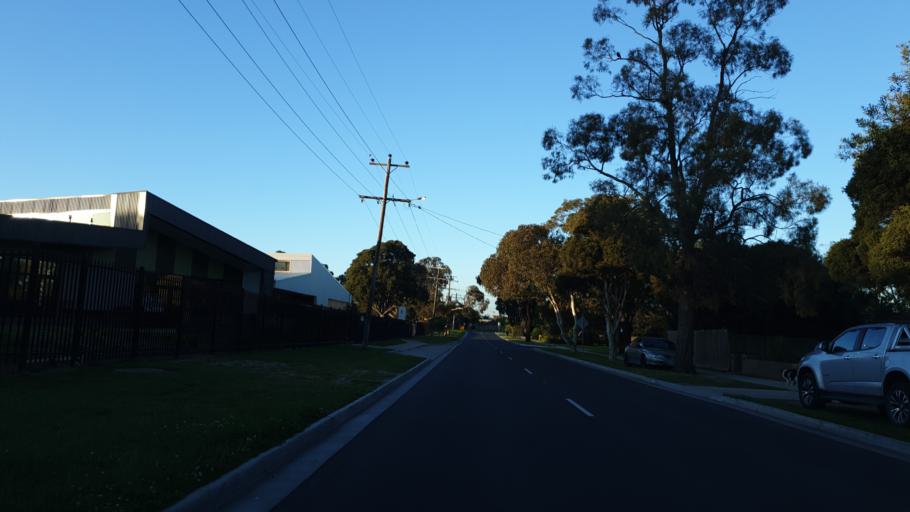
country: AU
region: Victoria
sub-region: Casey
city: Cranbourne
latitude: -38.1081
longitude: 145.2882
